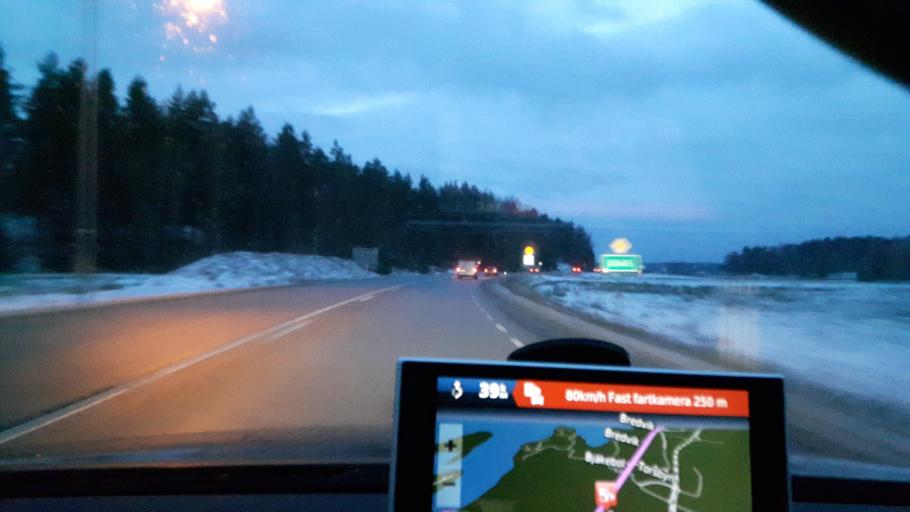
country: SE
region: Vaestra Goetaland
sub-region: Amals Kommun
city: Amal
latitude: 59.0141
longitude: 12.6916
